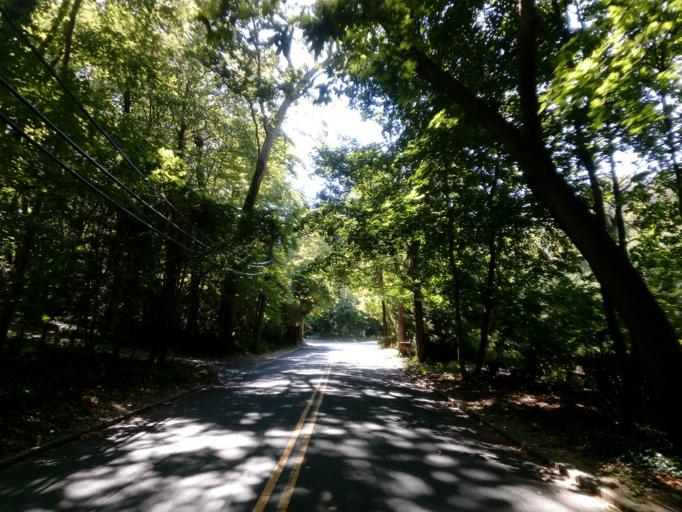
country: US
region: New York
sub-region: Nassau County
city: Laurel Hollow
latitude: 40.8690
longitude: -73.4819
